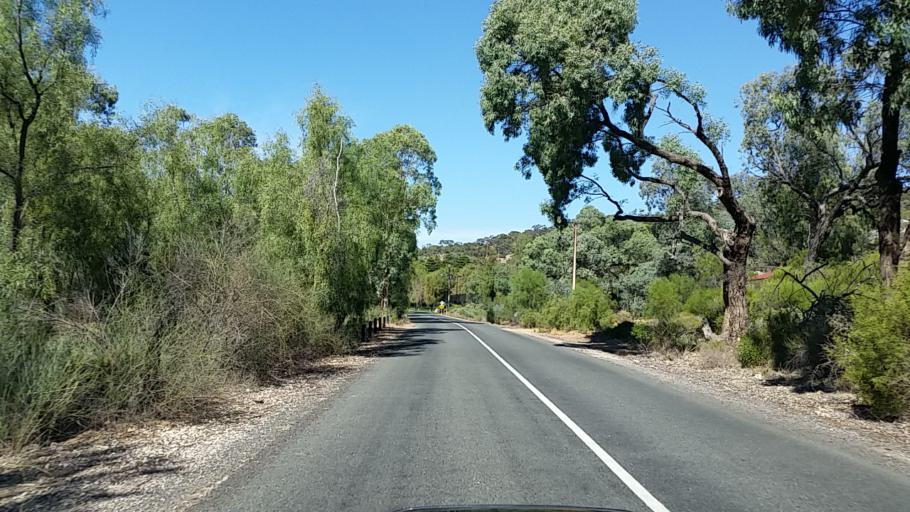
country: AU
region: South Australia
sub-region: Mid Murray
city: Mannum
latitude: -34.7368
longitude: 139.5373
